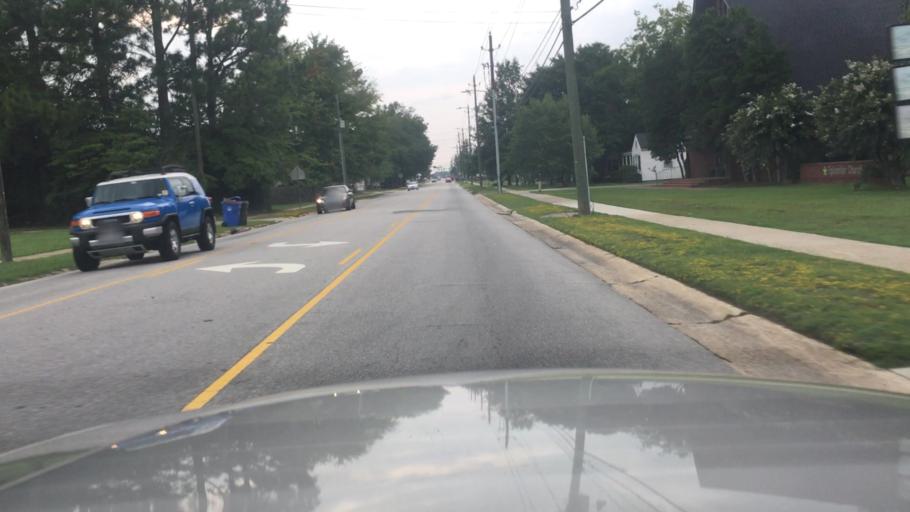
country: US
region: North Carolina
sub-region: Cumberland County
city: Fayetteville
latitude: 35.0679
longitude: -78.9185
